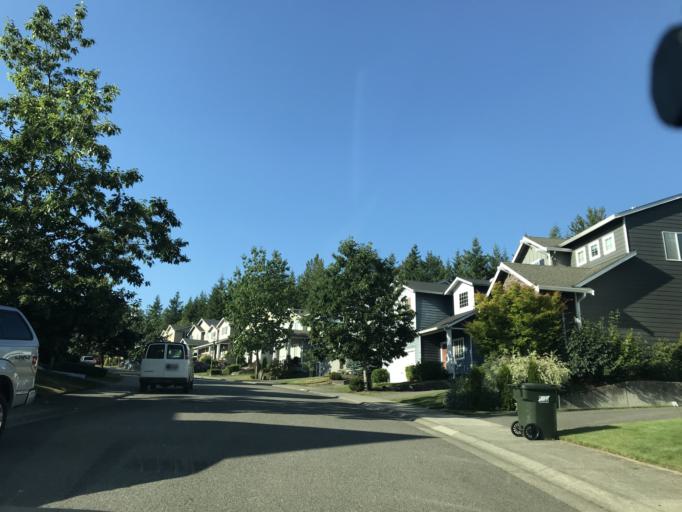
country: US
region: Washington
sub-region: King County
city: Ravensdale
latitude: 47.3520
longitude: -121.9991
